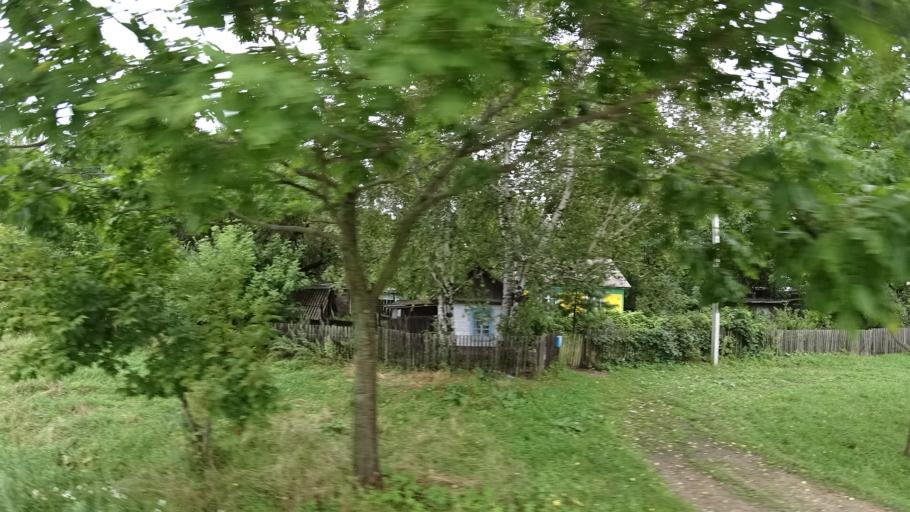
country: RU
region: Primorskiy
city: Monastyrishche
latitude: 44.0890
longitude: 132.5743
